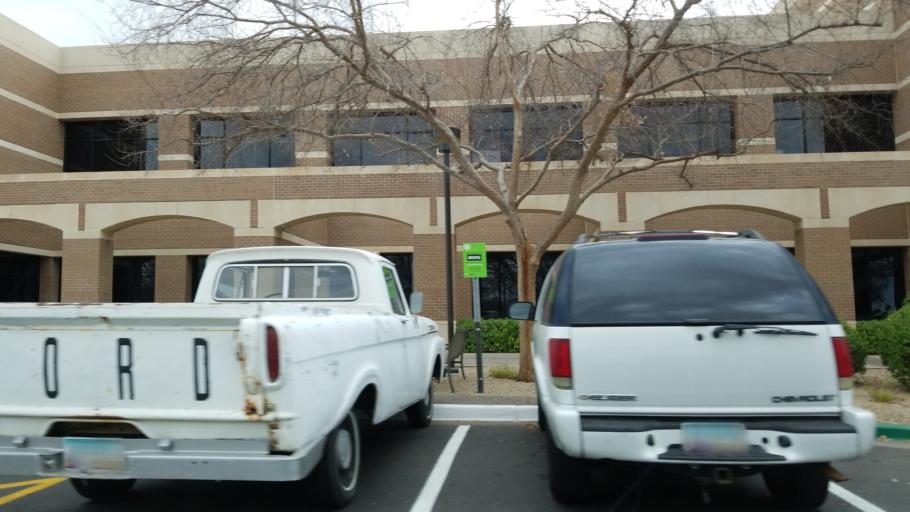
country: US
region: Arizona
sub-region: Maricopa County
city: Glendale
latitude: 33.6093
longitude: -112.1593
